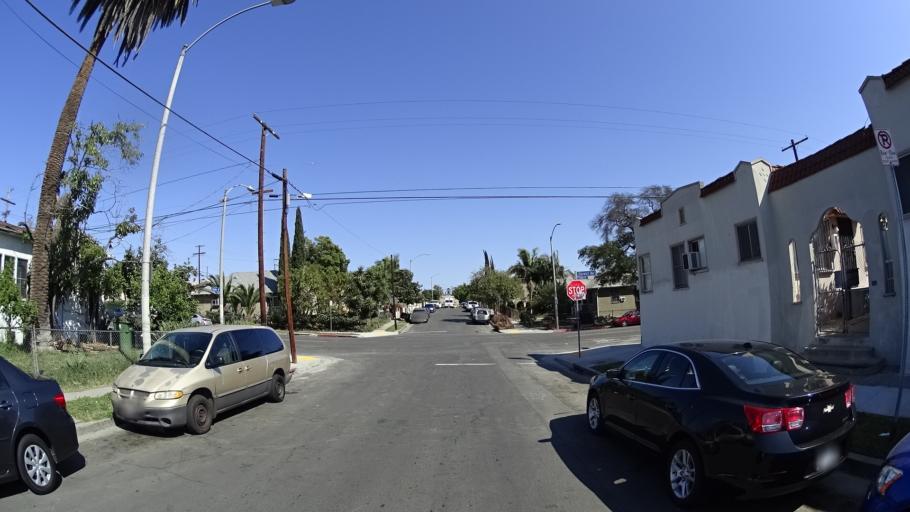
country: US
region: California
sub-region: Los Angeles County
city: Boyle Heights
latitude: 34.0467
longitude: -118.2008
